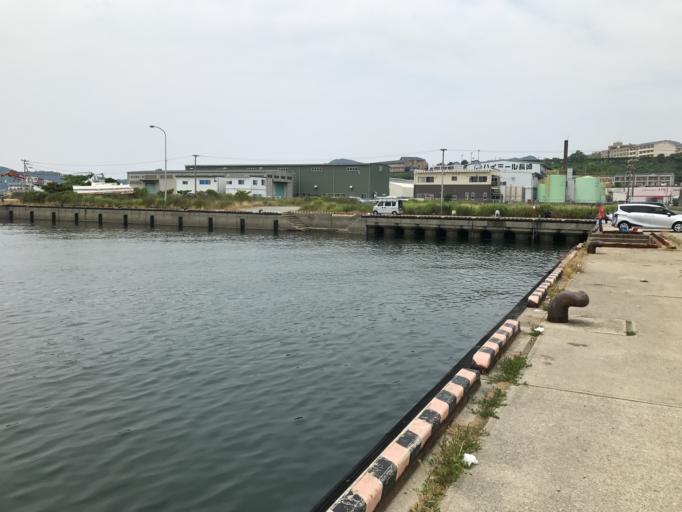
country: JP
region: Nagasaki
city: Togitsu
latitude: 32.8211
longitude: 129.7617
